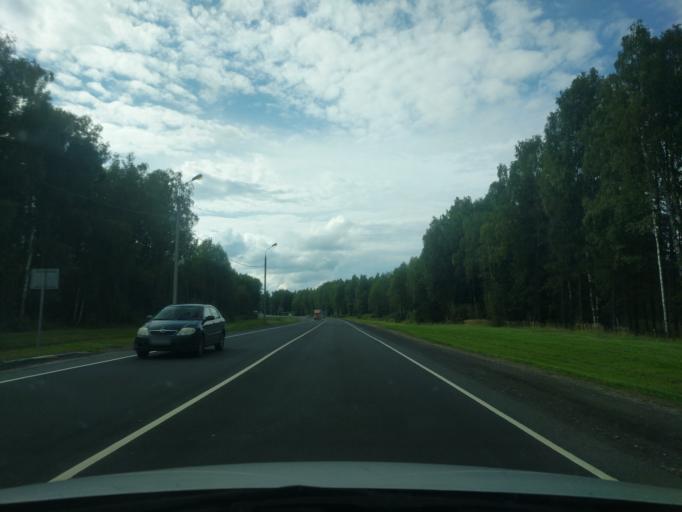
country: RU
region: Jaroslavl
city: Nekrasovskoye
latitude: 57.6367
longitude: 40.3990
